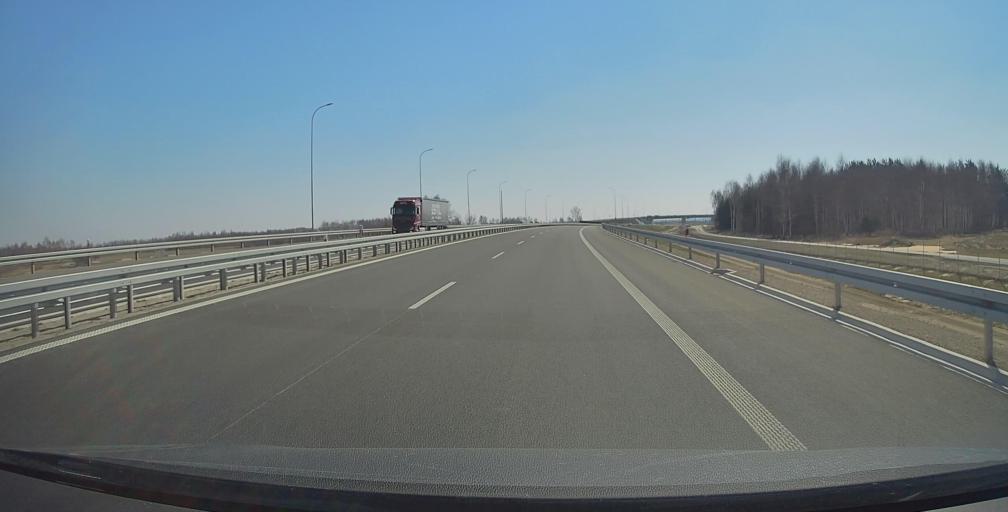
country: PL
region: Subcarpathian Voivodeship
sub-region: Powiat rzeszowski
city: Gorno
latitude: 50.2558
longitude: 22.1324
